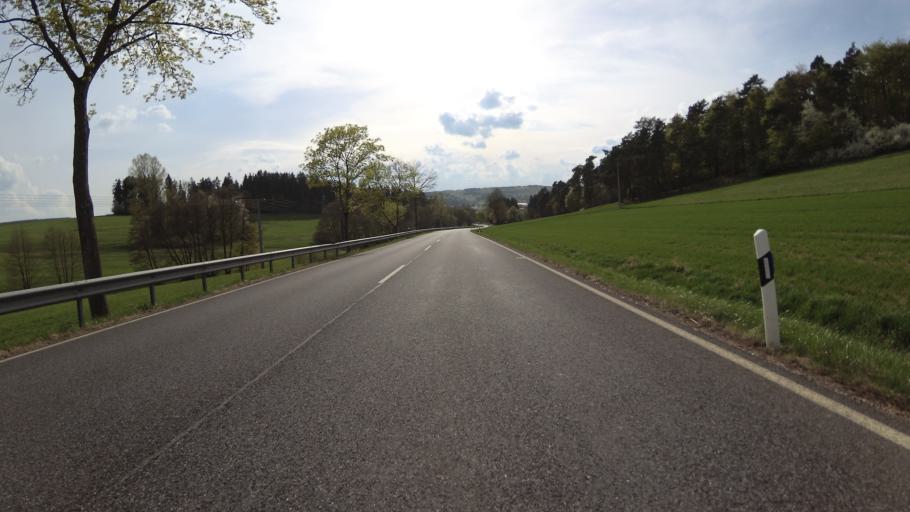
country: DE
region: Rheinland-Pfalz
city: Kelberg
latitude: 50.2889
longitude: 6.9343
